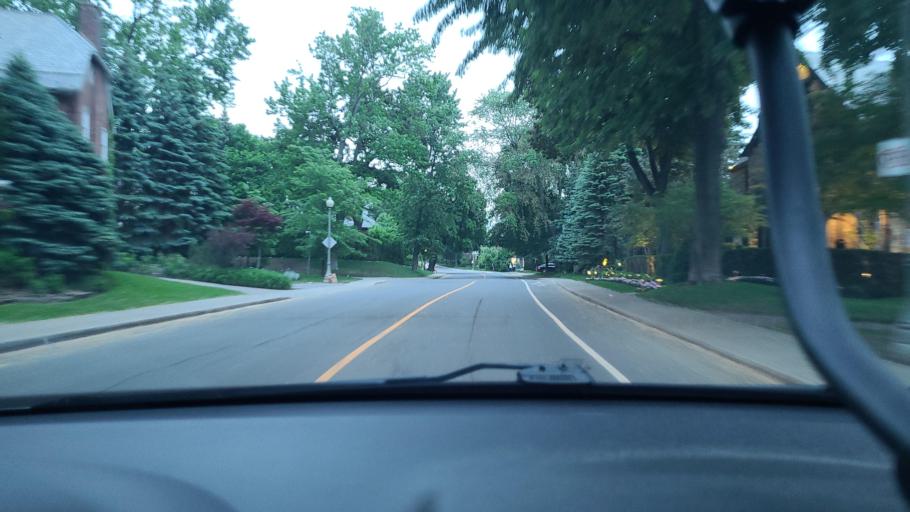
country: CA
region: Quebec
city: Westmount
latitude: 45.4861
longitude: -73.6056
